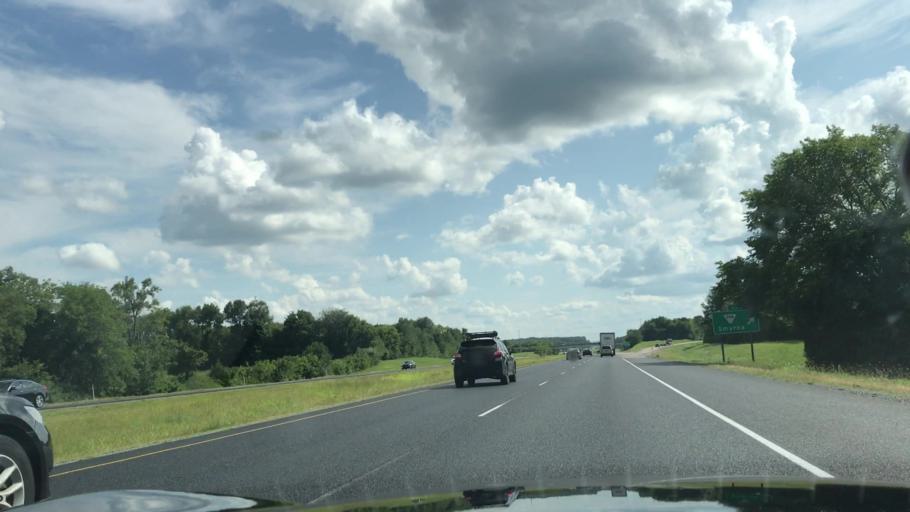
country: US
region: Tennessee
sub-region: Rutherford County
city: Smyrna
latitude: 35.9928
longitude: -86.4339
